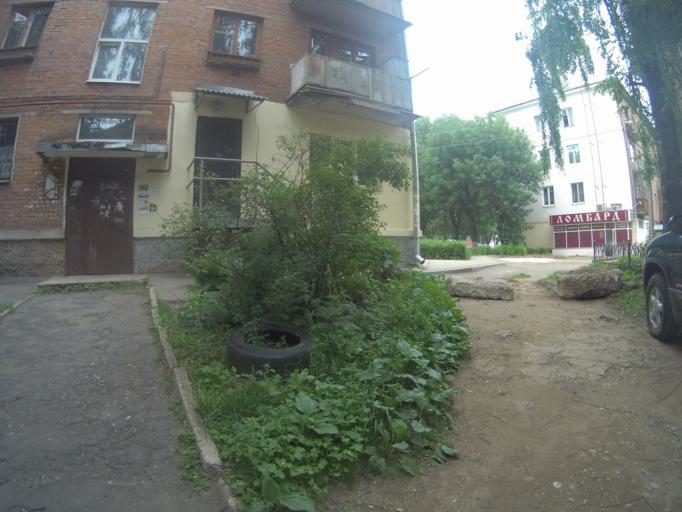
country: RU
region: Vladimir
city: Vladimir
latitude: 56.1415
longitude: 40.3899
